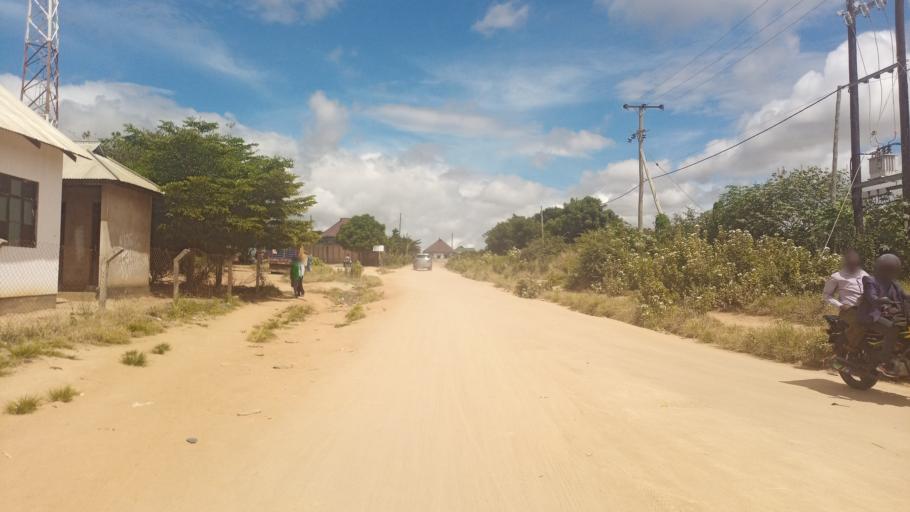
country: TZ
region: Dodoma
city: Dodoma
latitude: -6.1854
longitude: 35.7312
